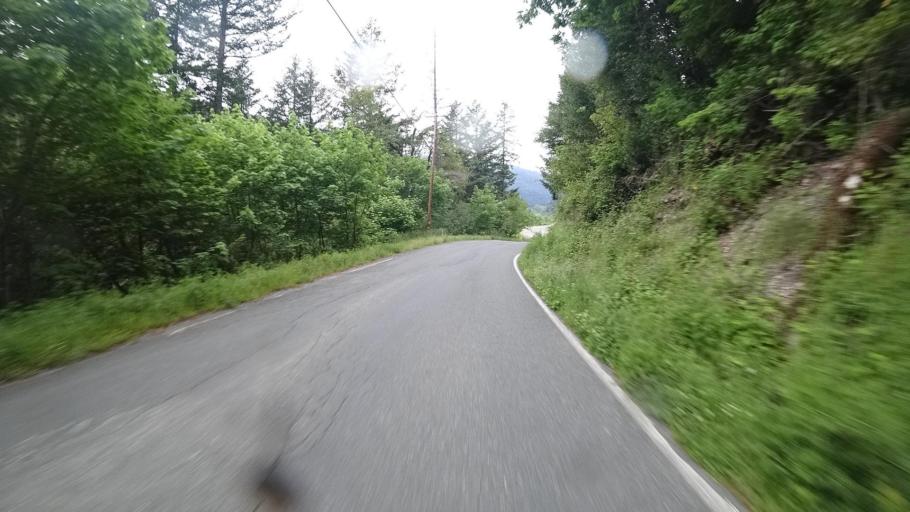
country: US
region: California
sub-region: Humboldt County
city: Willow Creek
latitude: 41.2057
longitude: -123.7532
